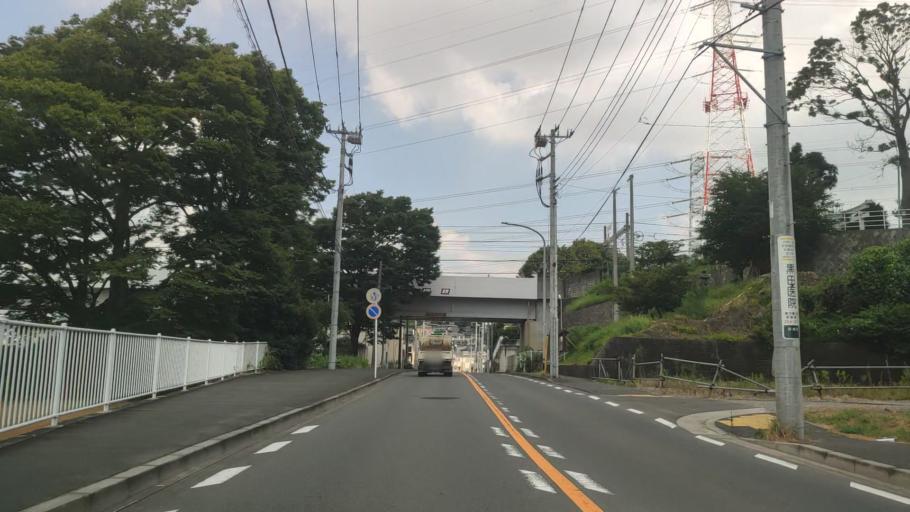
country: JP
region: Kanagawa
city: Minami-rinkan
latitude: 35.4310
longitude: 139.5133
